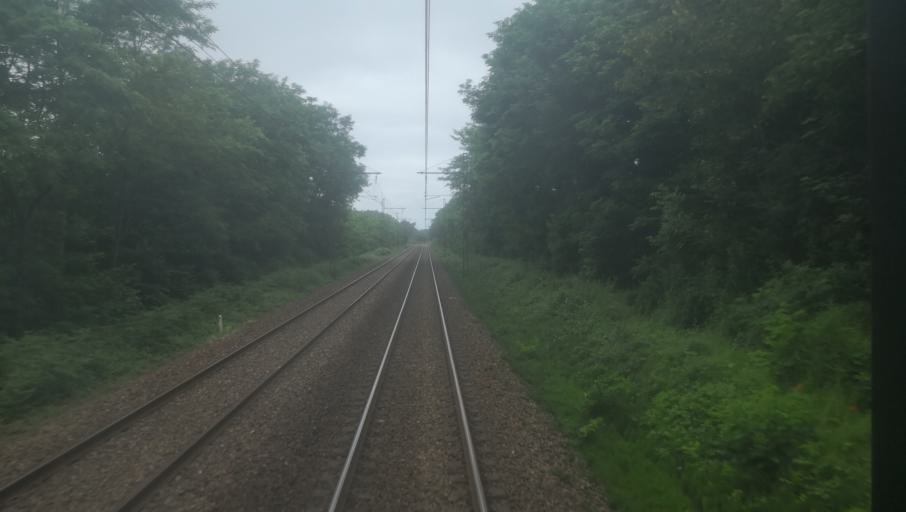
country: FR
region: Centre
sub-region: Departement de l'Indre
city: Le Pechereau
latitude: 46.4973
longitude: 1.5219
